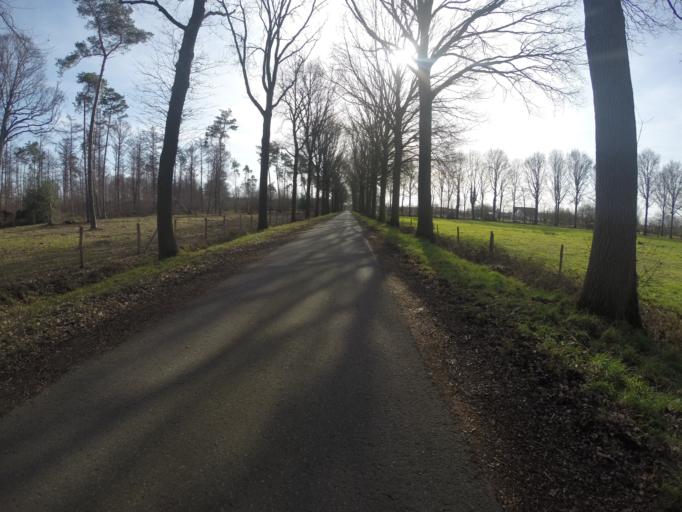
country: BE
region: Flanders
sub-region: Provincie West-Vlaanderen
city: Oostkamp
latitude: 51.1199
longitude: 3.2390
